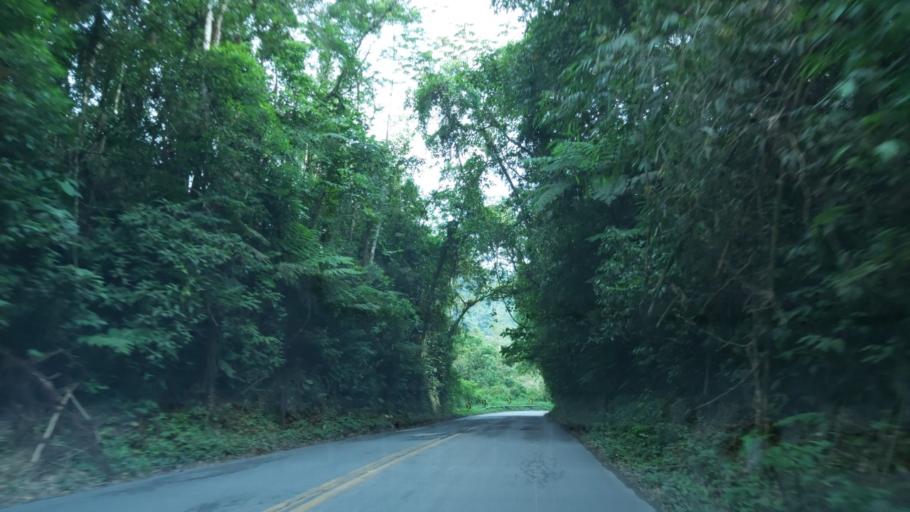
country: BR
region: Sao Paulo
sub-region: Juquia
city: Juquia
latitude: -24.0711
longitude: -47.6034
